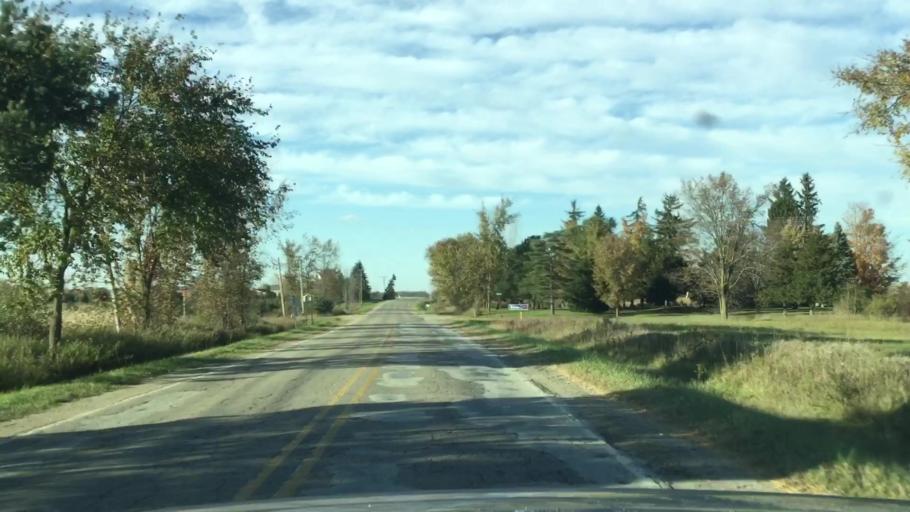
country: US
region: Michigan
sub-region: Lapeer County
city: North Branch
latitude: 43.2373
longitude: -83.1965
